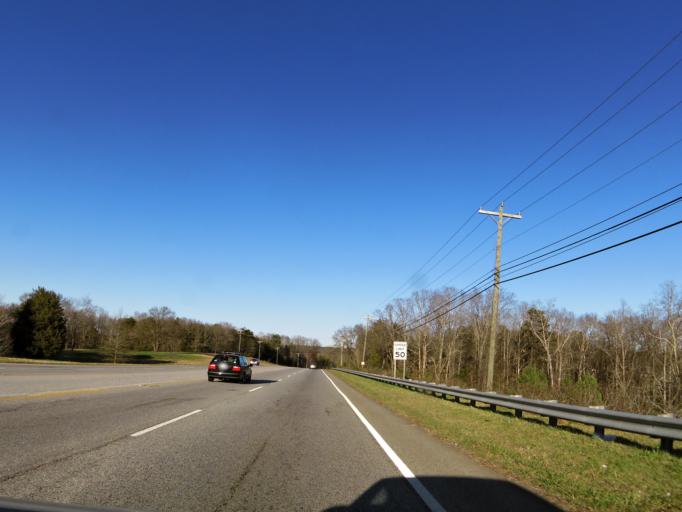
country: US
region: South Carolina
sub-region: Spartanburg County
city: Fairforest
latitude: 34.9018
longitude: -82.0347
